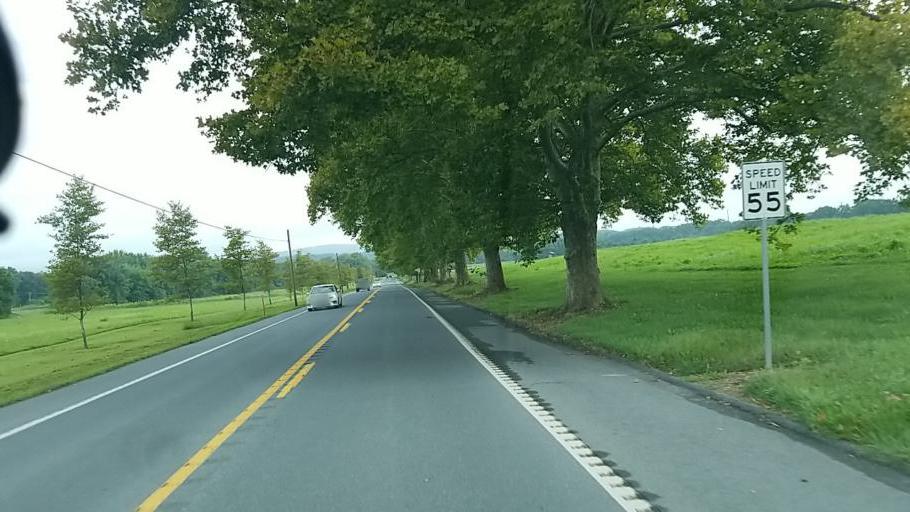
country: US
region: Pennsylvania
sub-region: Dauphin County
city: Matamoras
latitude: 40.4759
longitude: -76.9315
